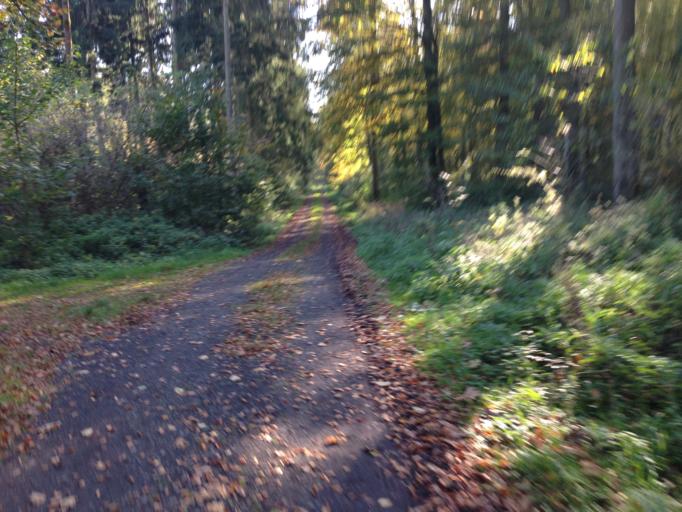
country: DE
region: Hesse
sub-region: Regierungsbezirk Giessen
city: Grossen Buseck
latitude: 50.5703
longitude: 8.7779
